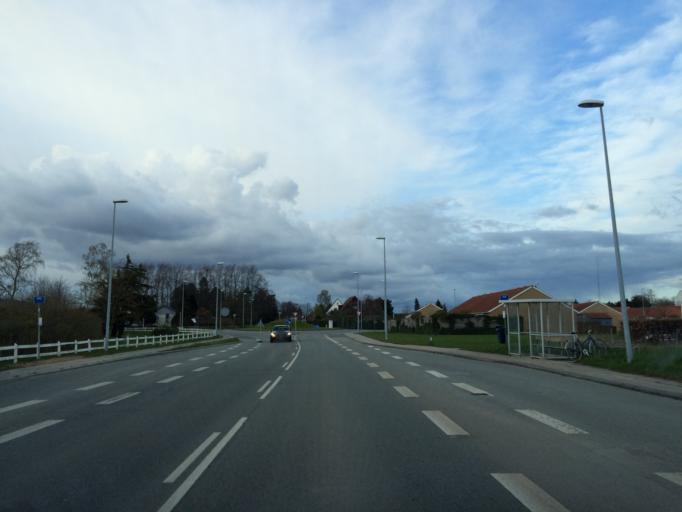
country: DK
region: South Denmark
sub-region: Odense Kommune
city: Bellinge
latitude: 55.3121
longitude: 10.3115
